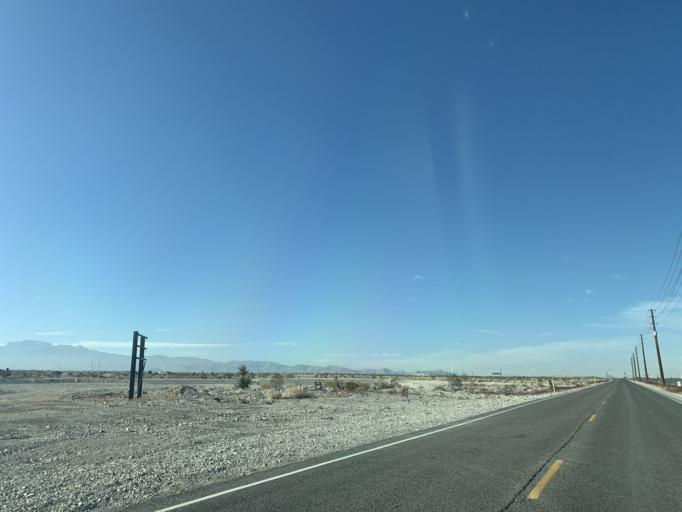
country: US
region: Nevada
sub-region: Clark County
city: Summerlin South
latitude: 36.3204
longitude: -115.3069
